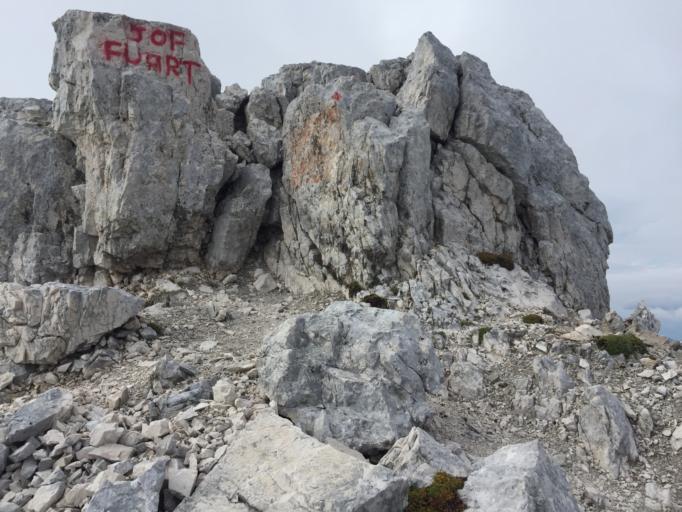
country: IT
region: Friuli Venezia Giulia
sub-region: Provincia di Udine
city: Malborghetto
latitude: 46.4298
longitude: 13.4912
